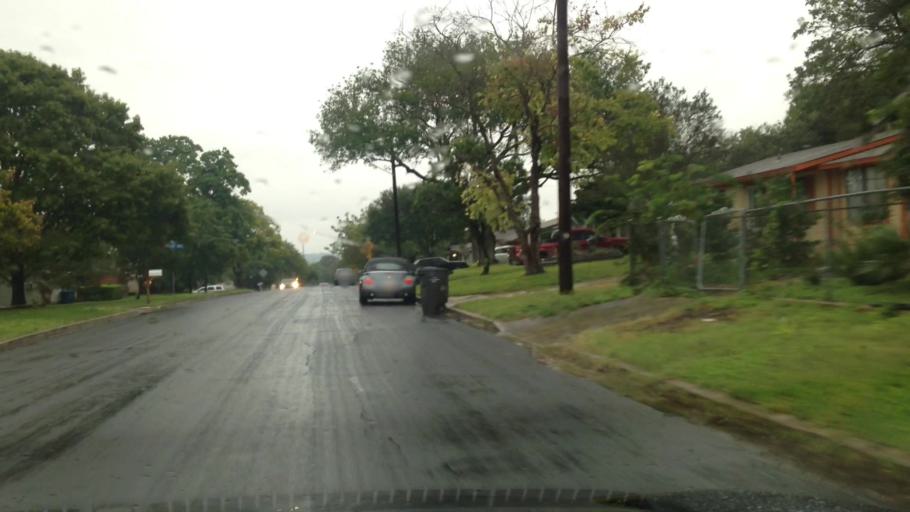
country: US
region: Texas
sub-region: Bexar County
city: Balcones Heights
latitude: 29.5146
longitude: -98.5438
